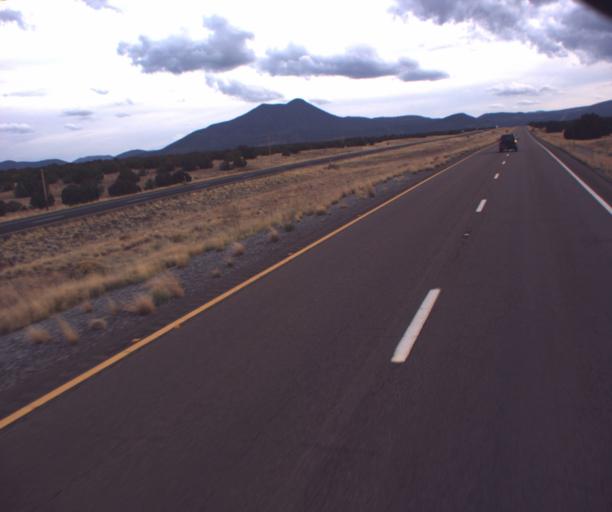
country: US
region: Arizona
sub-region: Coconino County
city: Flagstaff
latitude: 35.4864
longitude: -111.5558
